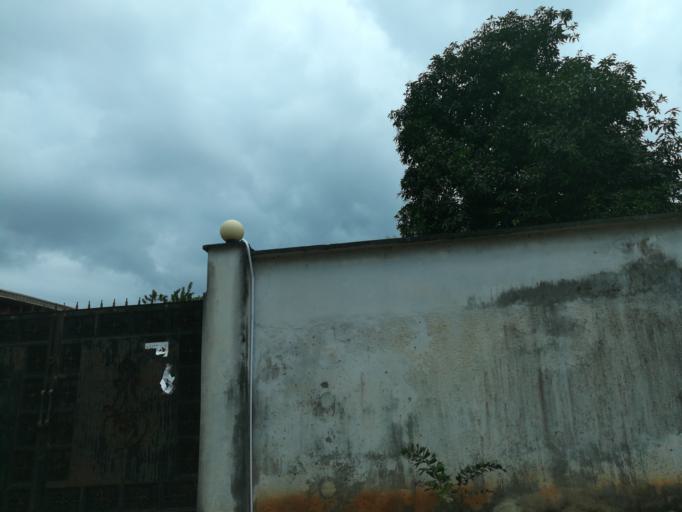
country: NG
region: Lagos
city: Oshodi
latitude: 6.5552
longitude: 3.3269
